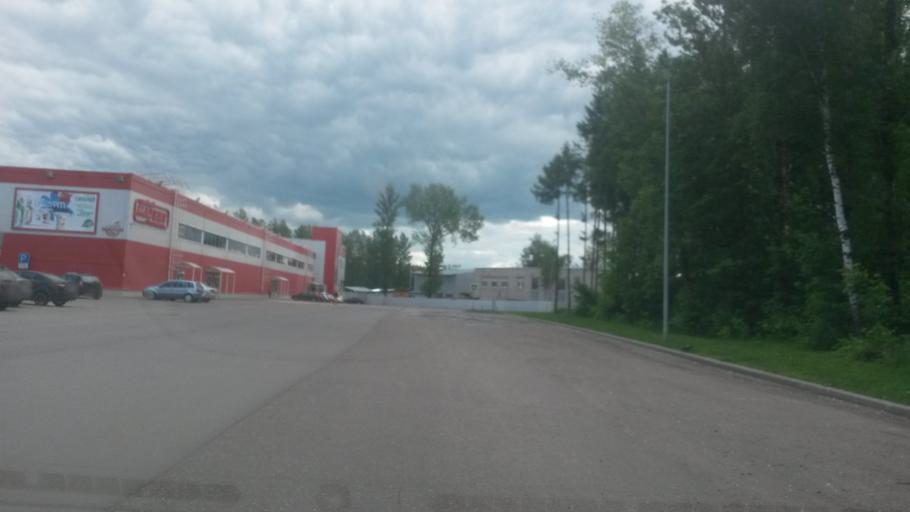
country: RU
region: Jaroslavl
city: Yaroslavl
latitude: 57.6784
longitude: 39.8039
